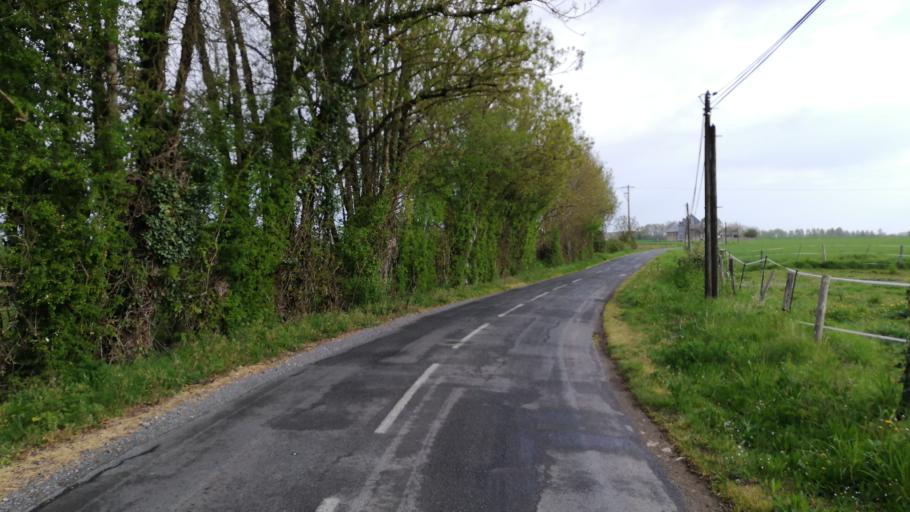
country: FR
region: Pays de la Loire
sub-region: Departement de la Vendee
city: Maillezais
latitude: 46.3277
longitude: -0.7124
